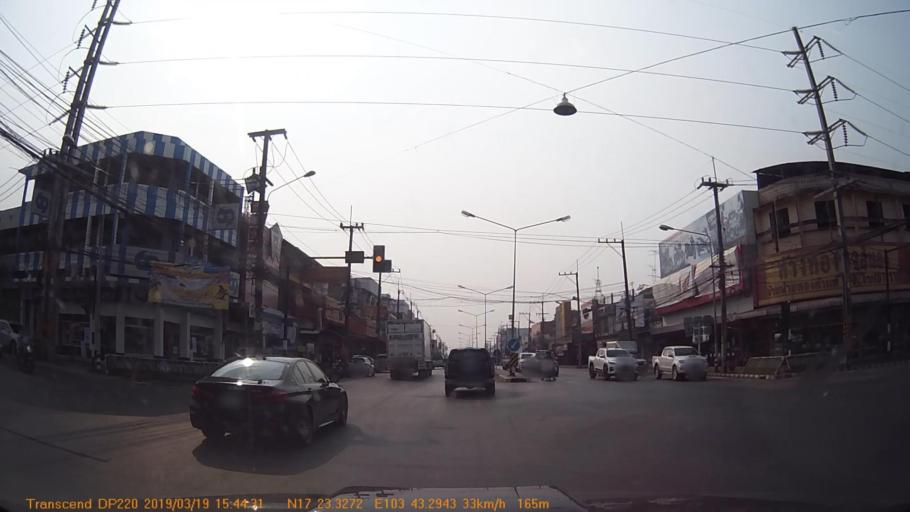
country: TH
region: Sakon Nakhon
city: Phang Khon
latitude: 17.3888
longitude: 103.7215
